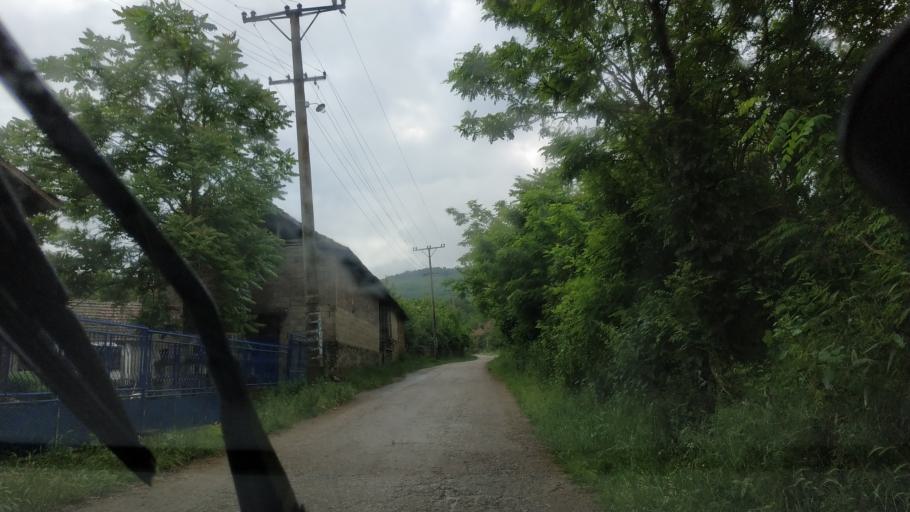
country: RS
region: Central Serbia
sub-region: Nisavski Okrug
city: Aleksinac
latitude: 43.4312
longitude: 21.6508
